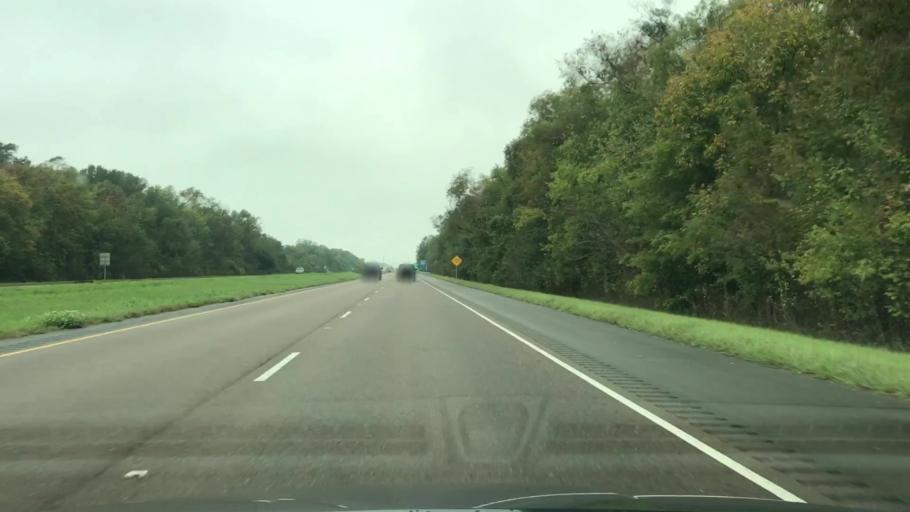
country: US
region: Louisiana
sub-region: Terrebonne Parish
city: Gray
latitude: 29.6842
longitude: -90.7361
